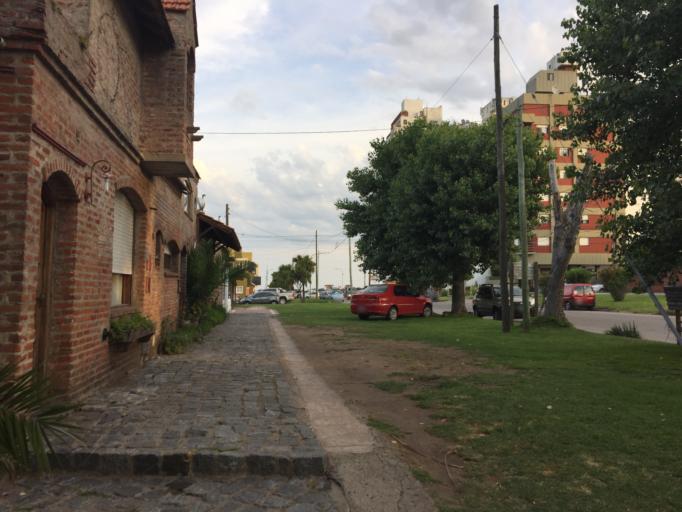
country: AR
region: Buenos Aires
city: Miramar
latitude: -38.2685
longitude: -57.8298
